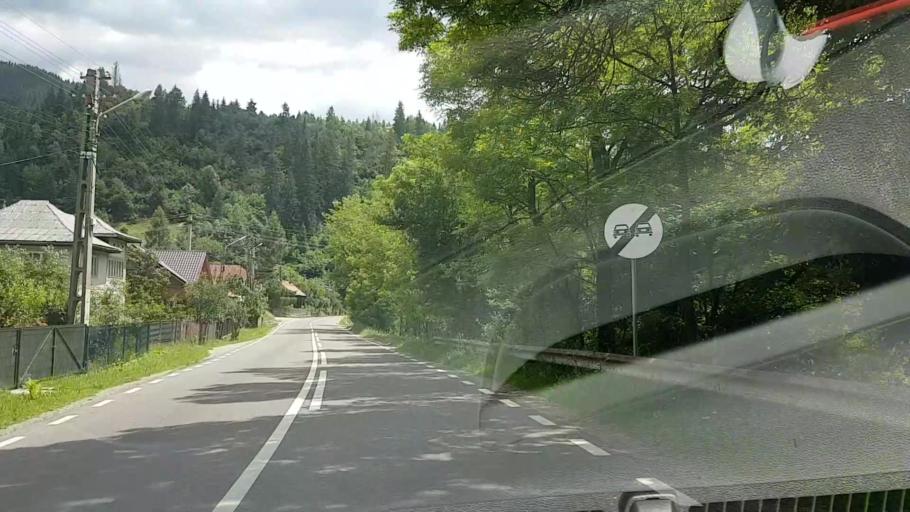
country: RO
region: Suceava
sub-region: Comuna Brosteni
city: Brosteni
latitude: 47.2550
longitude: 25.6931
